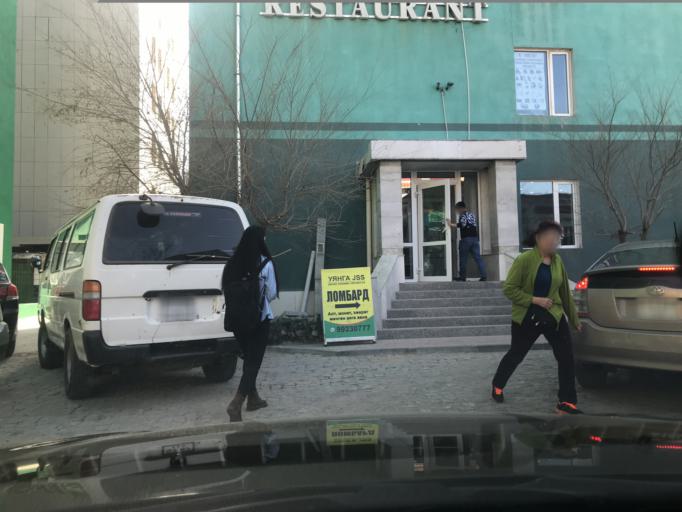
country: MN
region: Ulaanbaatar
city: Ulaanbaatar
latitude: 47.9205
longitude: 106.9013
